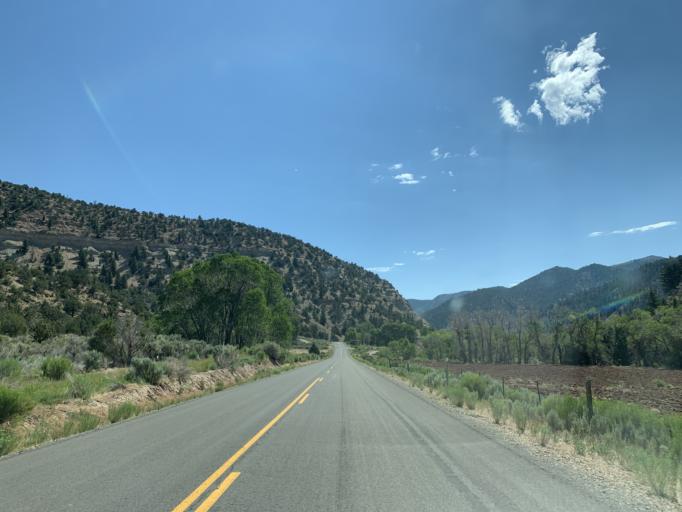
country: US
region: Utah
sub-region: Carbon County
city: East Carbon City
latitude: 39.7764
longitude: -110.4717
